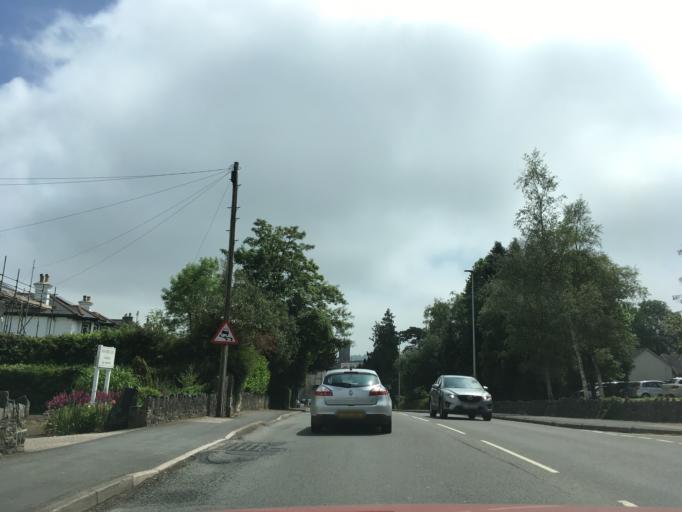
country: GB
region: England
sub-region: Devon
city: Totnes
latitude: 50.4361
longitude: -3.6926
